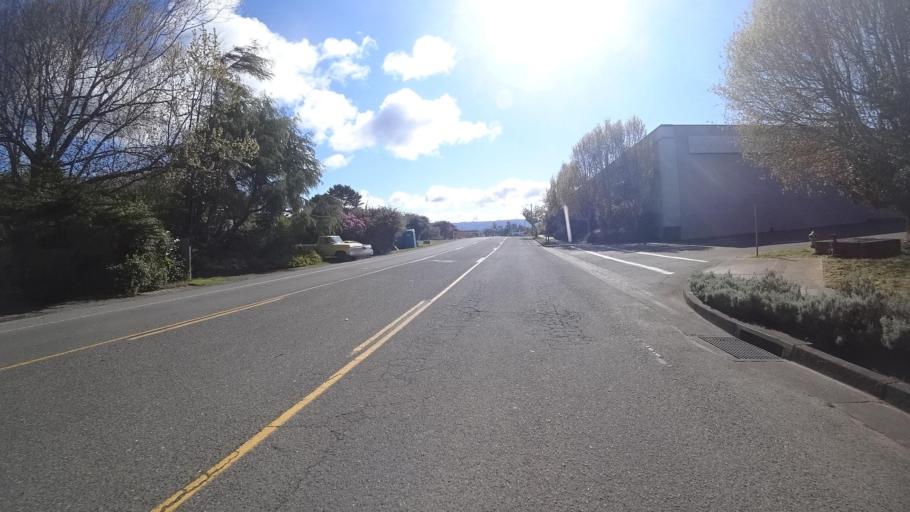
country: US
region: California
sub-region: Humboldt County
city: McKinleyville
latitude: 40.9342
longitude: -124.1039
